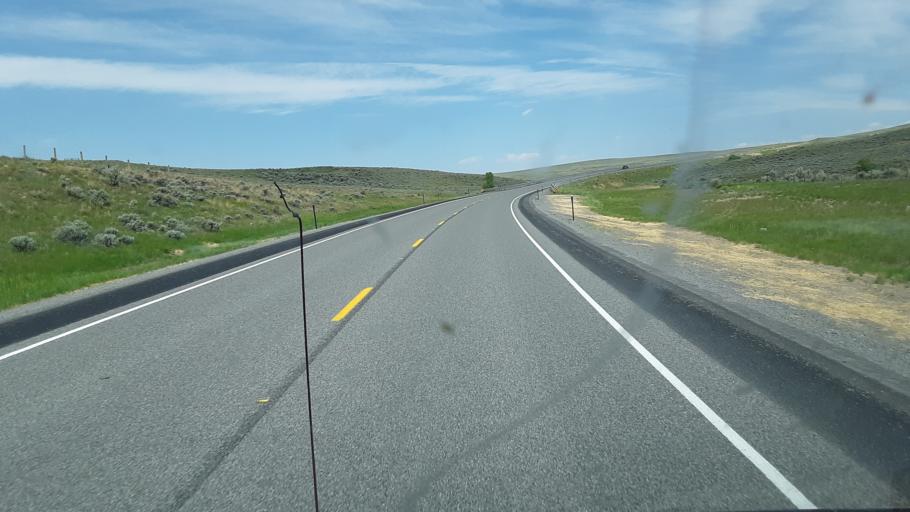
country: US
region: Wyoming
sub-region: Park County
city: Cody
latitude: 44.2497
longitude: -108.8565
